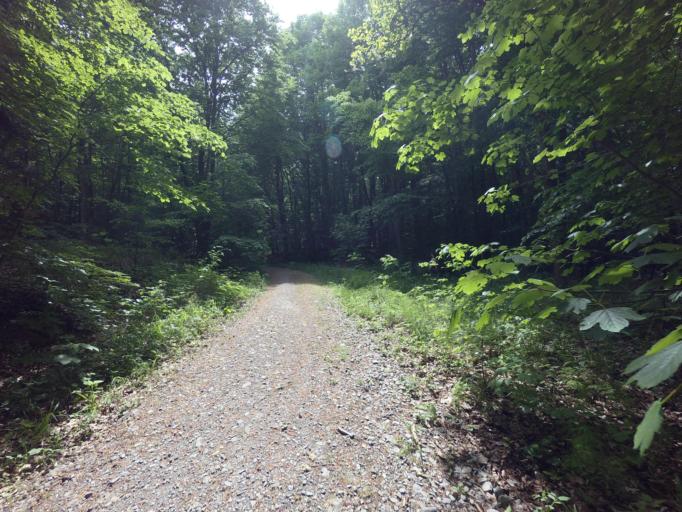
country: DE
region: Lower Saxony
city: Kneitlingen
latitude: 52.2021
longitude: 10.7598
